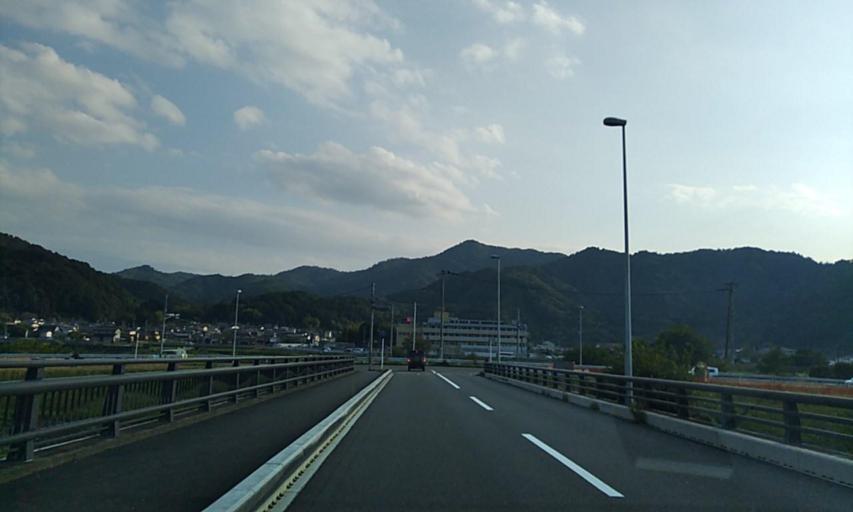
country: JP
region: Kyoto
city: Ayabe
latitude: 35.3072
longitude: 135.2048
